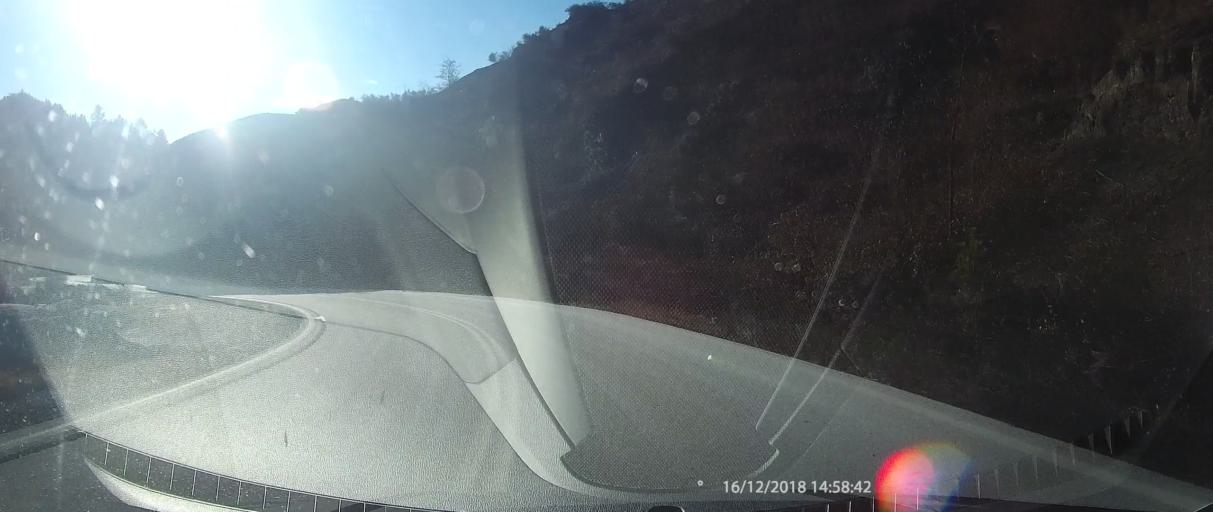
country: GR
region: West Macedonia
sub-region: Nomos Kastorias
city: Nestorio
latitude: 40.2231
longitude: 21.0282
